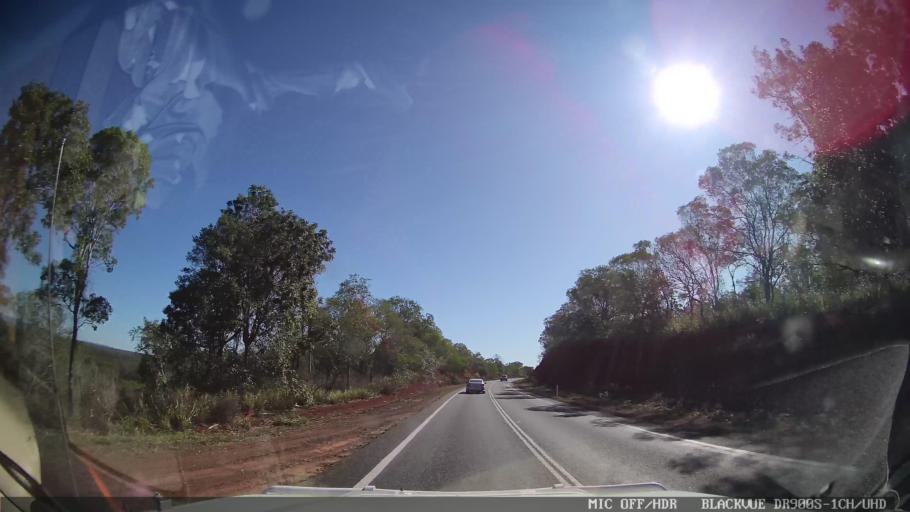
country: AU
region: Queensland
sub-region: Bundaberg
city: Childers
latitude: -25.2376
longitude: 152.2558
